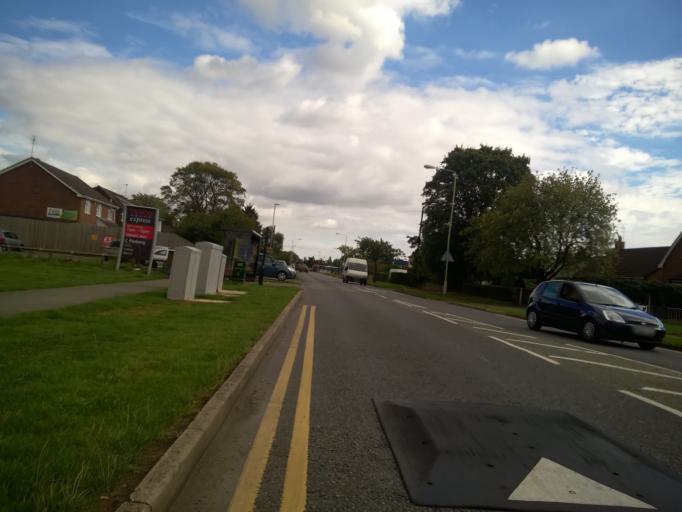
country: GB
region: England
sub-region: Leicestershire
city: Glenfield
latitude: 52.6453
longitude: -1.1936
